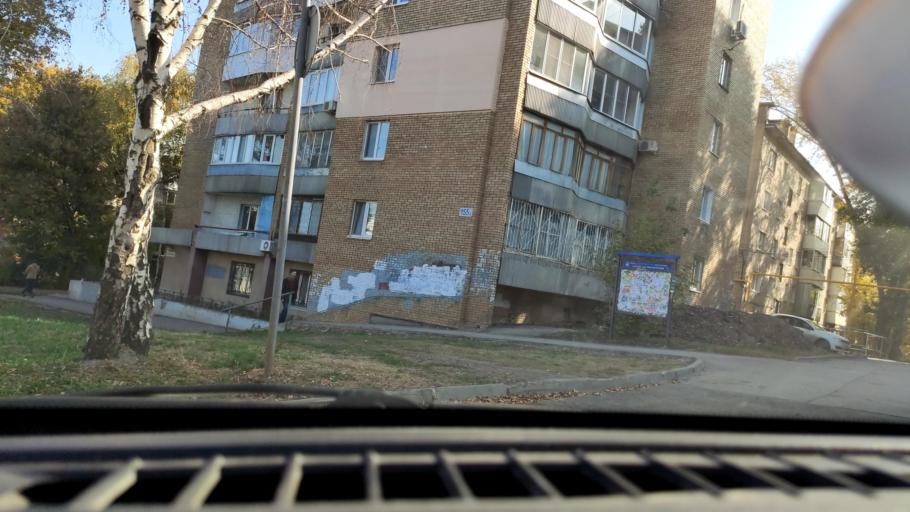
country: RU
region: Samara
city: Samara
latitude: 53.1974
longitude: 50.2094
